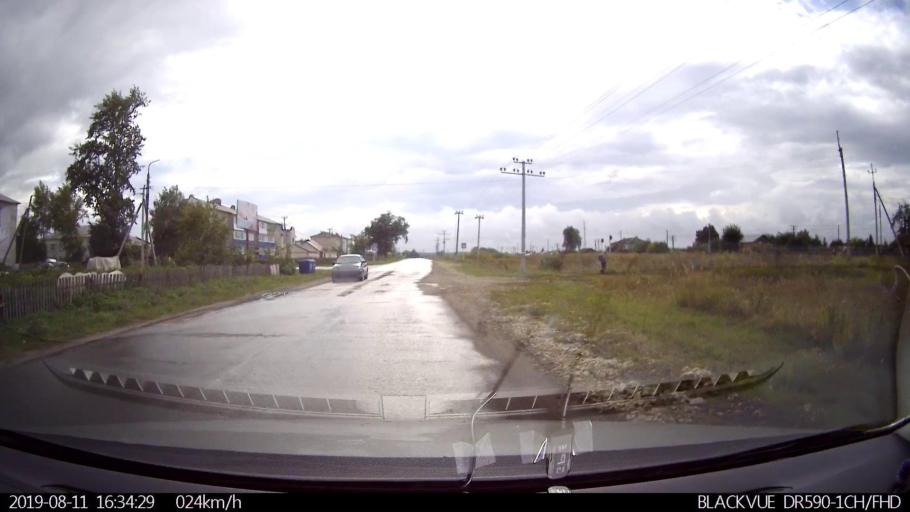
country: RU
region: Ulyanovsk
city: Mayna
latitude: 54.1163
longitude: 47.6214
